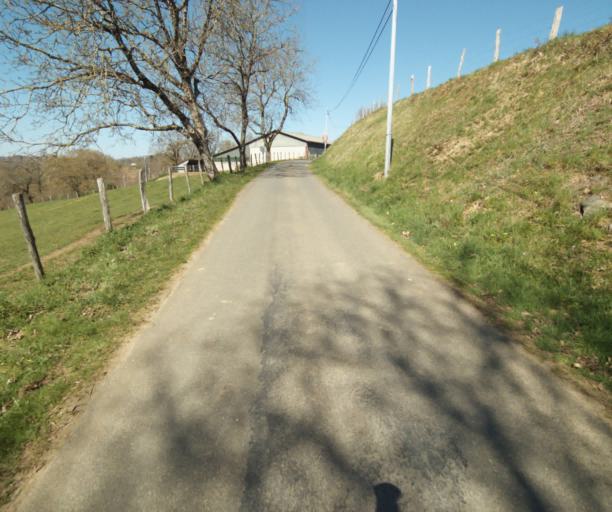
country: FR
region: Limousin
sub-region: Departement de la Correze
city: Saint-Clement
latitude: 45.3229
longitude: 1.7097
